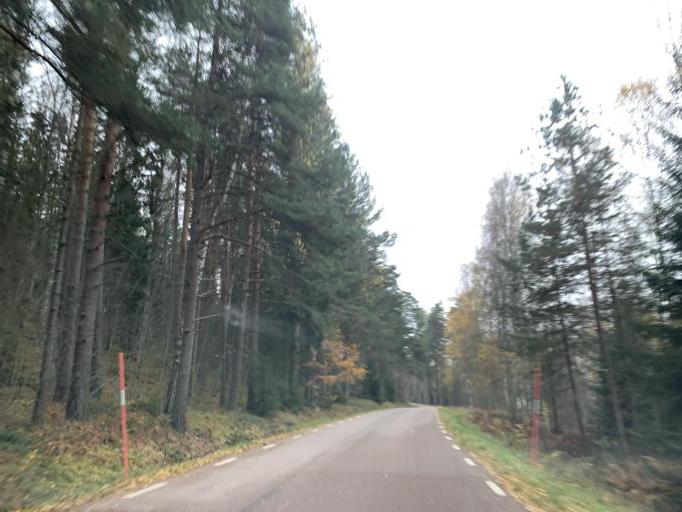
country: SE
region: Vaestmanland
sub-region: Surahammars Kommun
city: Surahammar
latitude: 59.6885
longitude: 16.0847
